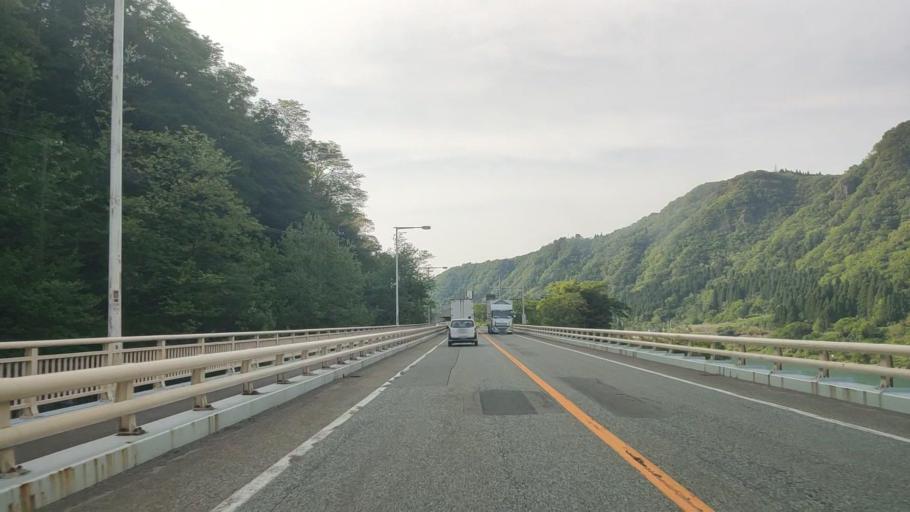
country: JP
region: Toyama
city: Yatsuomachi-higashikumisaka
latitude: 36.5449
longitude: 137.2280
